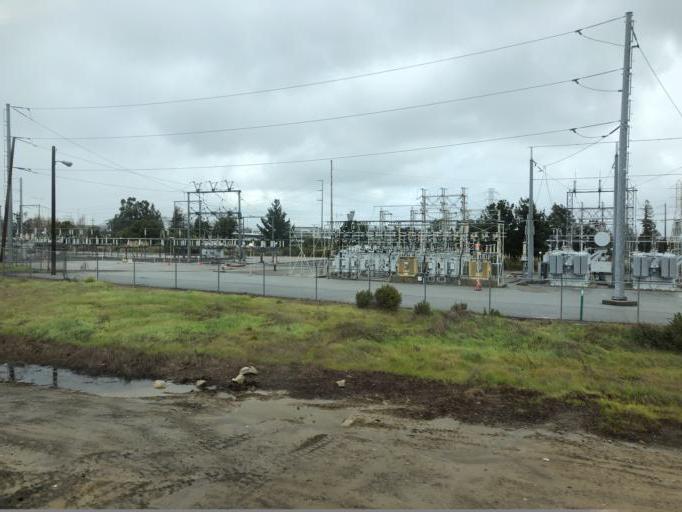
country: US
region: California
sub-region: San Mateo County
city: Millbrae
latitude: 37.6047
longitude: -122.3916
